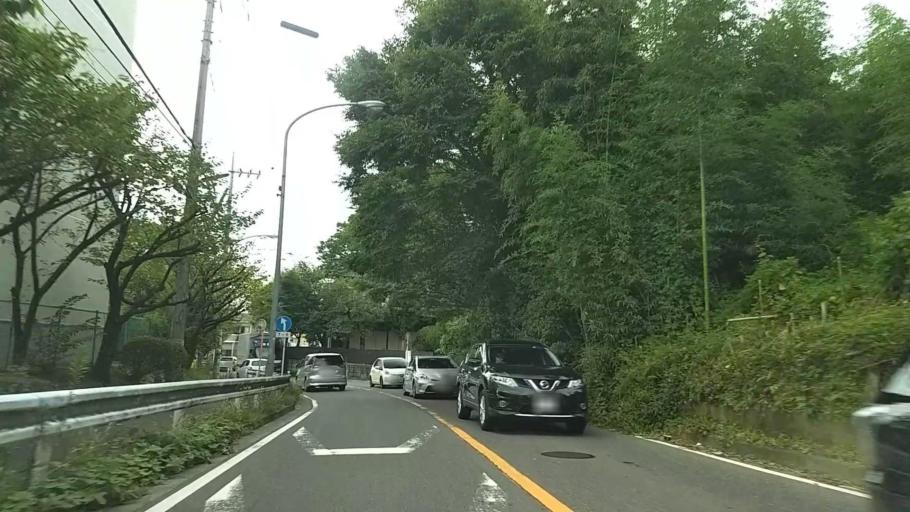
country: JP
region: Kanagawa
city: Yokohama
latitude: 35.5028
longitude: 139.5642
